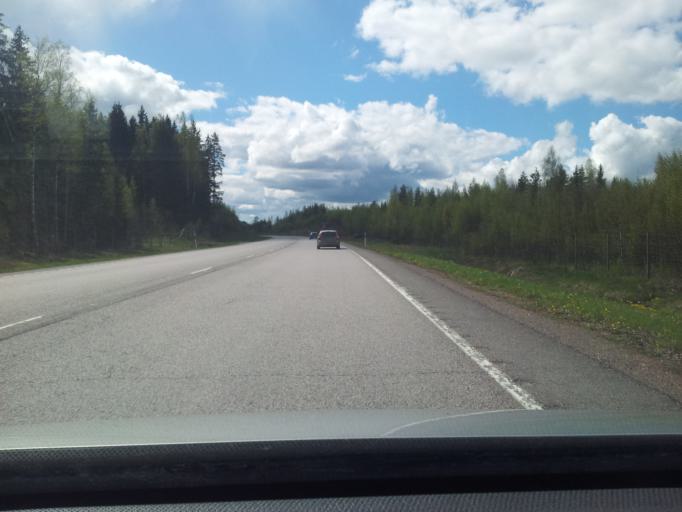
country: FI
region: Uusimaa
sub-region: Loviisa
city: Liljendal
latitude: 60.5239
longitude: 25.9664
